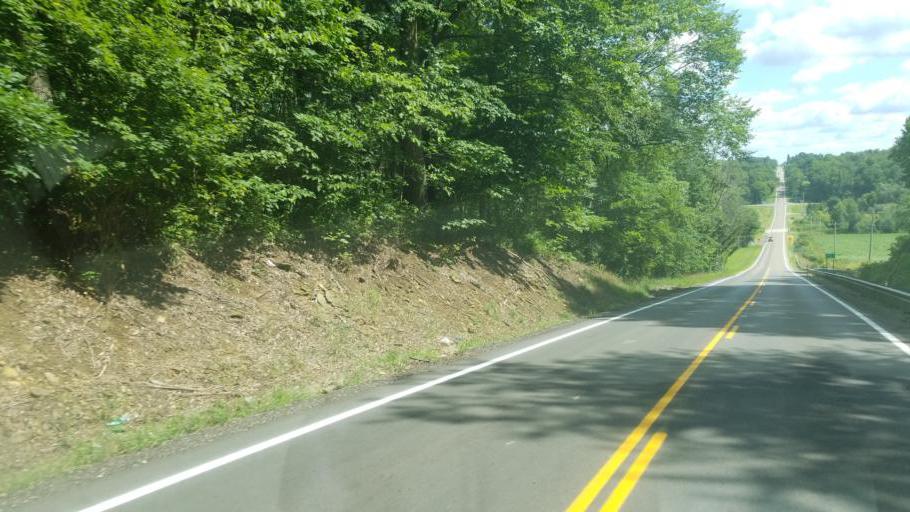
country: US
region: Ohio
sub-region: Richland County
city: Lexington
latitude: 40.7109
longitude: -82.6659
